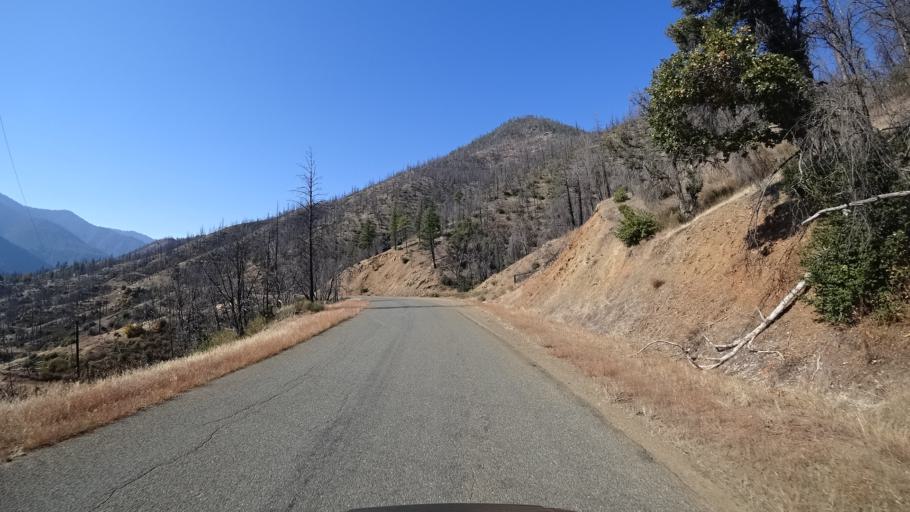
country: US
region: California
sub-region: Siskiyou County
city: Happy Camp
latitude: 41.7256
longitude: -123.0164
